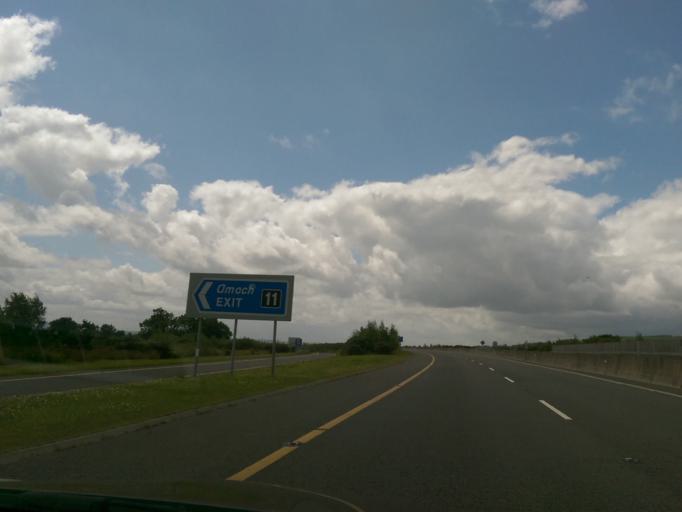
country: IE
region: Munster
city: Cahir
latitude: 52.3579
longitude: -7.9962
